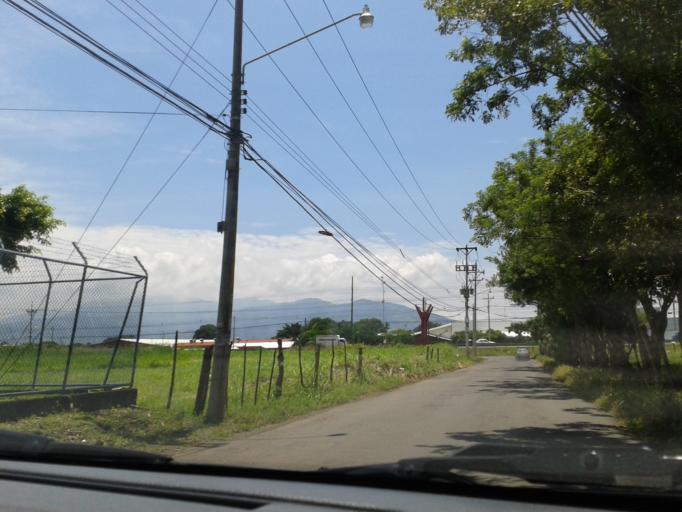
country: CR
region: Alajuela
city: Alajuela
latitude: 9.9962
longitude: -84.2341
